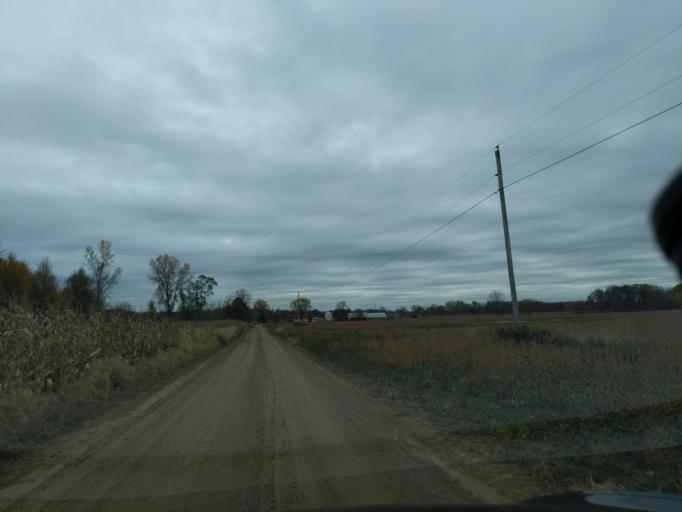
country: US
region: Michigan
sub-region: Eaton County
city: Eaton Rapids
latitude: 42.4255
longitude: -84.6005
